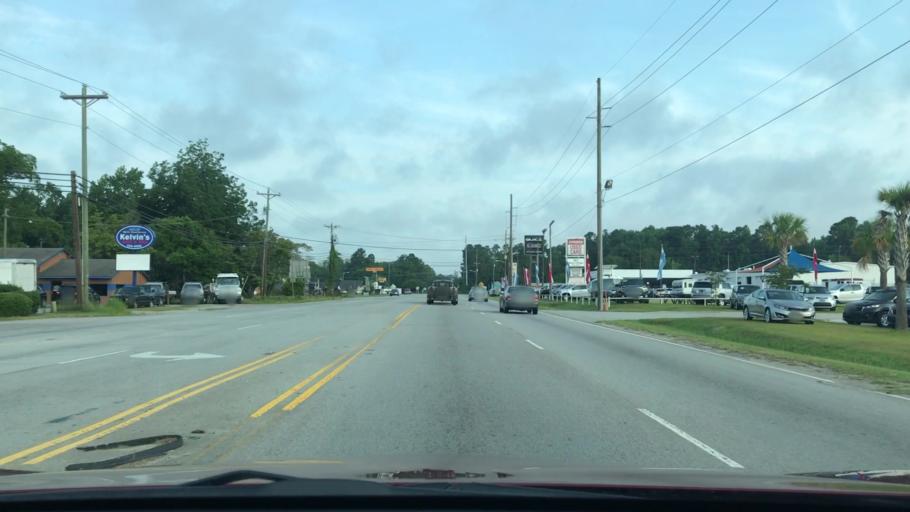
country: US
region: South Carolina
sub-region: Orangeburg County
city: Wilkinson Heights
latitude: 33.4859
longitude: -80.8320
